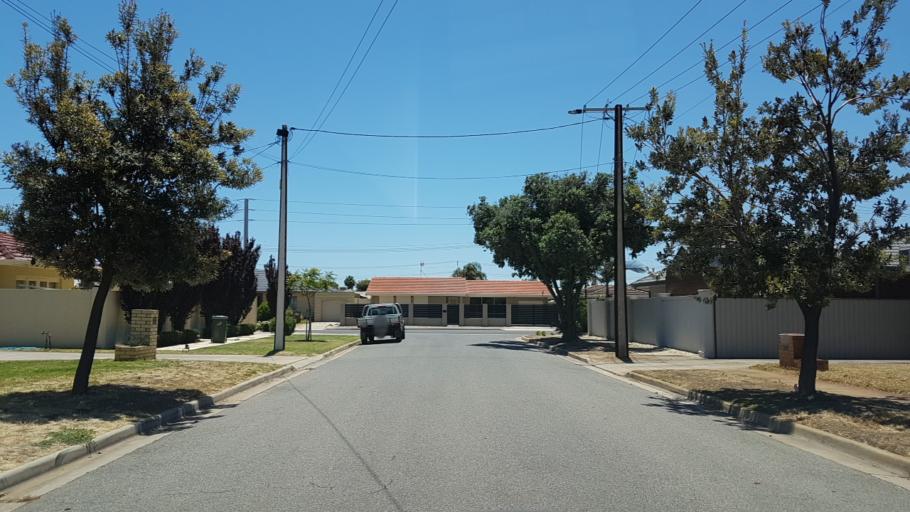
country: AU
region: South Australia
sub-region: Charles Sturt
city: West Lakes Shore
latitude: -34.8579
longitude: 138.4845
